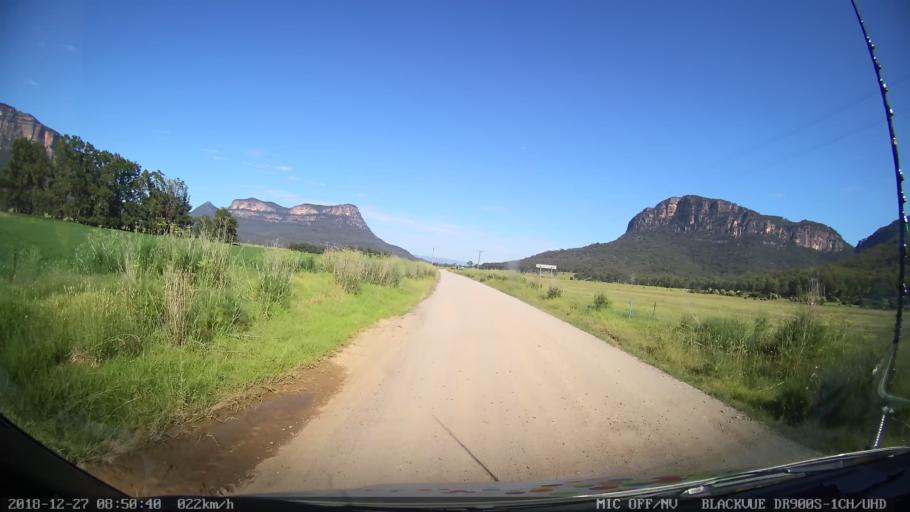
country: AU
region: New South Wales
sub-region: Lithgow
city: Portland
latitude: -33.1198
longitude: 150.2759
